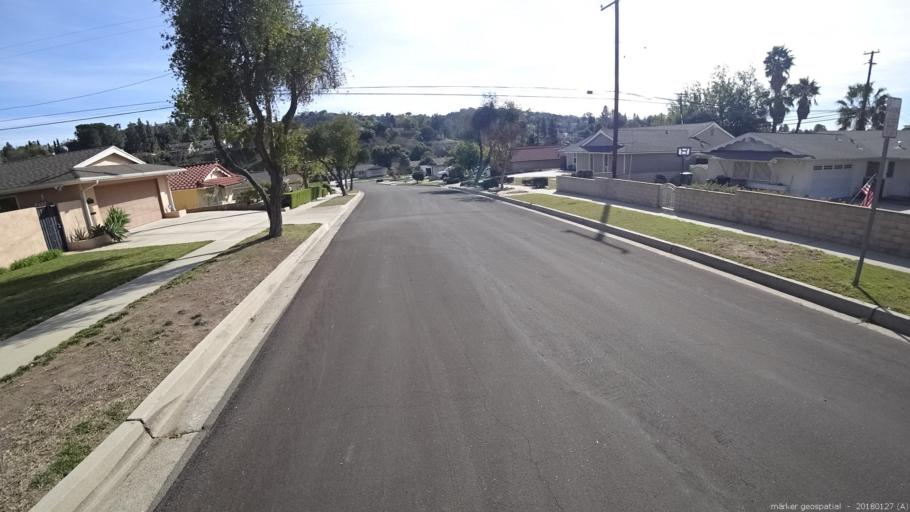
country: US
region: California
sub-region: Los Angeles County
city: Diamond Bar
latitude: 34.0263
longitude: -117.8000
